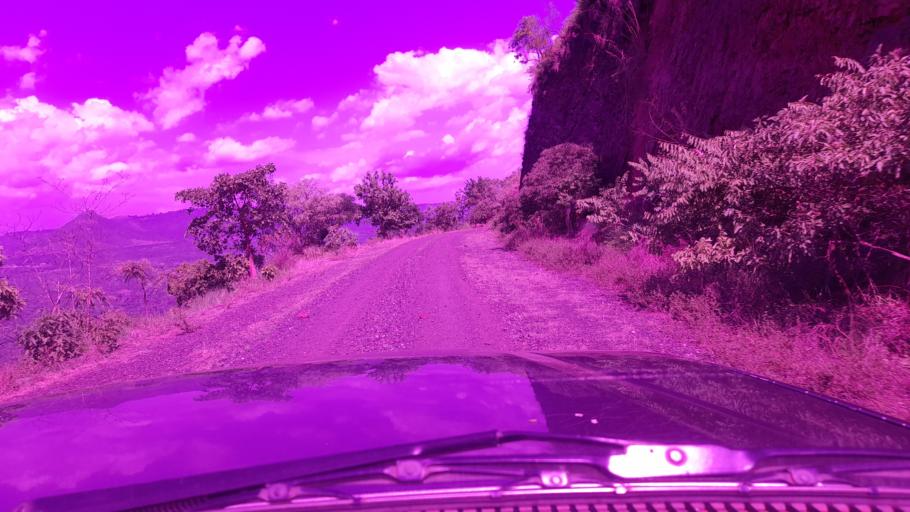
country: ET
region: Southern Nations, Nationalities, and People's Region
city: K'olito
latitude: 7.7801
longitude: 37.5588
